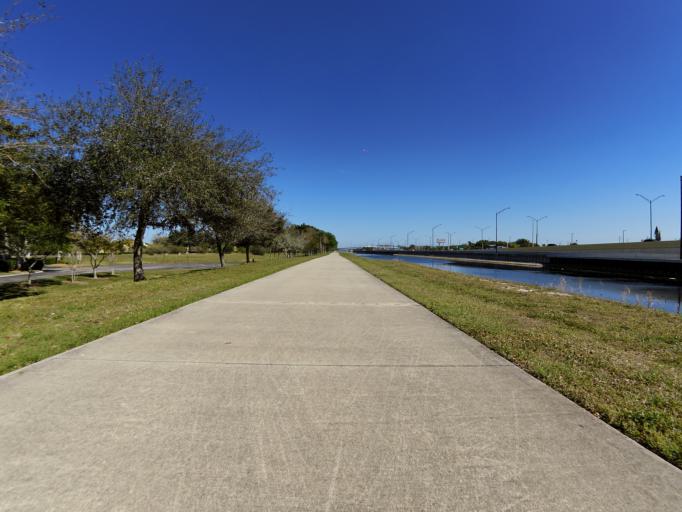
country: US
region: Florida
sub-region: Broward County
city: Pine Island Ridge
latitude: 26.1031
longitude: -80.2626
